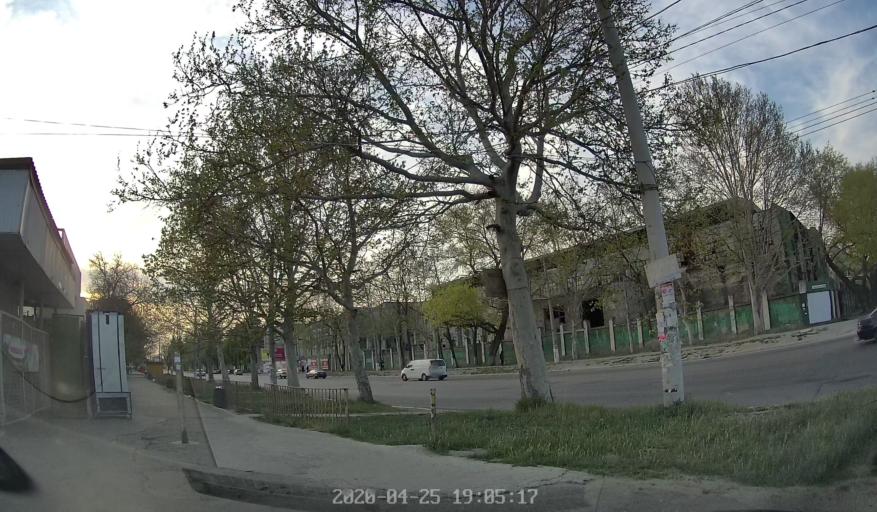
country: GR
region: South Aegean
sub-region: Nomos Kykladon
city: Serifos
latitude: 37.1750
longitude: 24.5400
